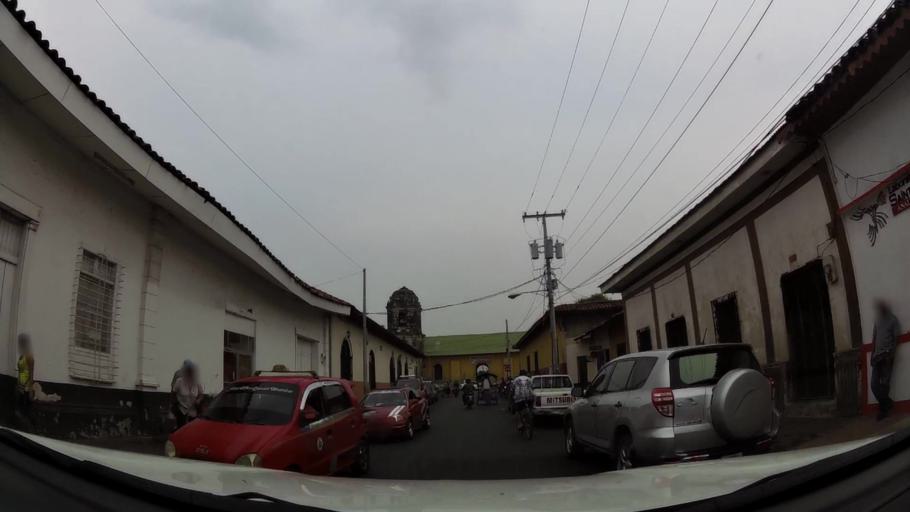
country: NI
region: Leon
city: Leon
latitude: 12.4388
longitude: -86.8748
